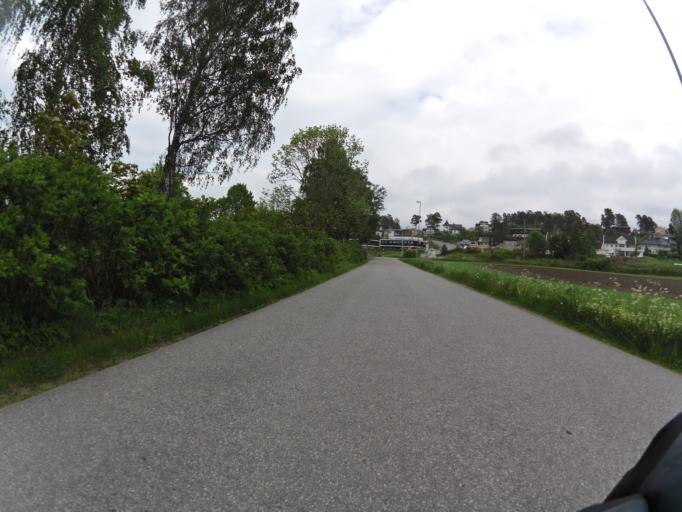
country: NO
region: Ostfold
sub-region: Moss
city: Moss
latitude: 59.4094
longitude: 10.6559
